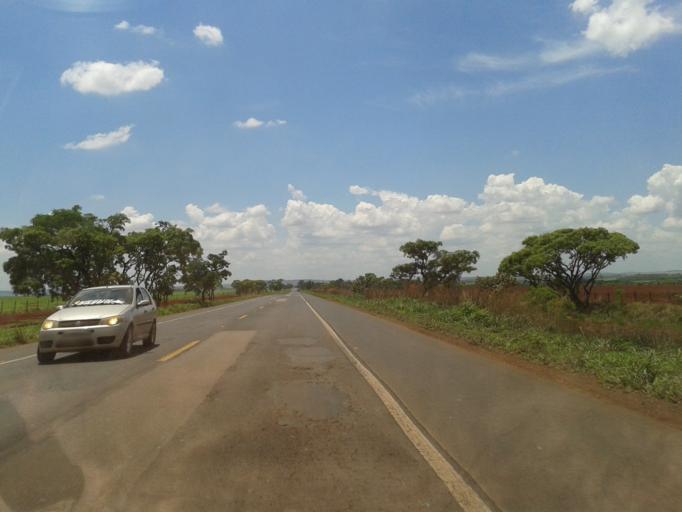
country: BR
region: Goias
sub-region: Goiatuba
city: Goiatuba
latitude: -18.2807
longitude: -49.6225
